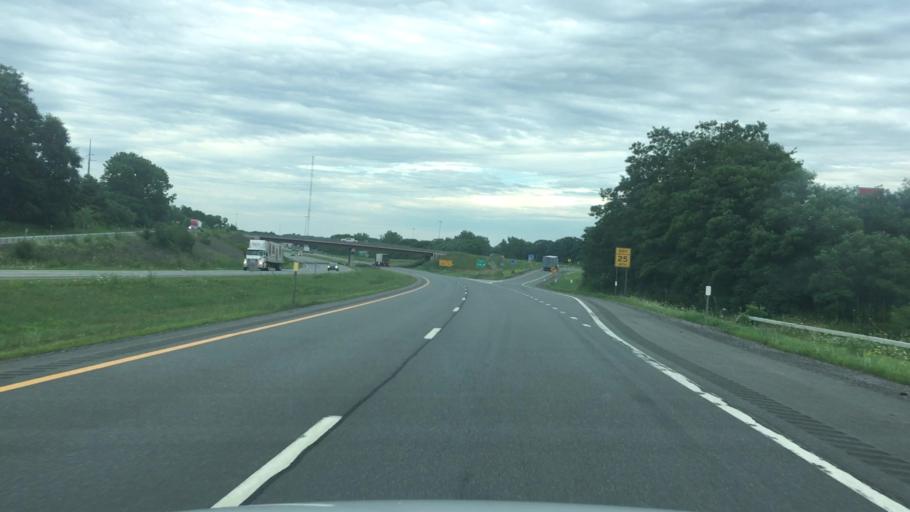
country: US
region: New York
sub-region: Schenectady County
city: Rotterdam
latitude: 42.7824
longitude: -74.0313
